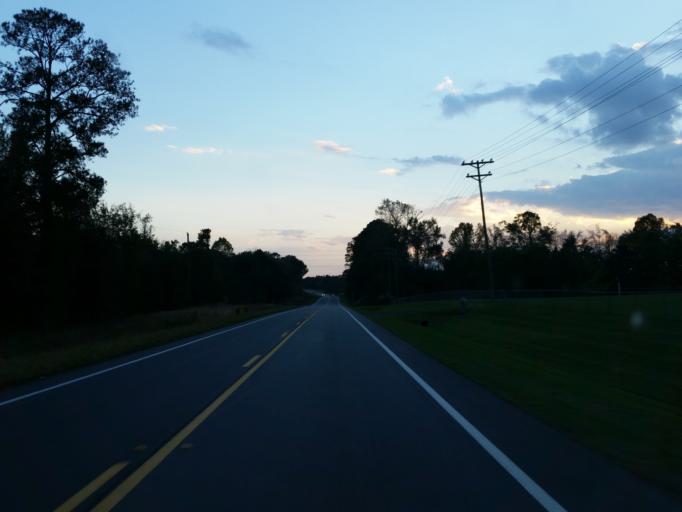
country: US
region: Georgia
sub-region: Pulaski County
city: Hawkinsville
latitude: 32.2577
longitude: -83.4907
